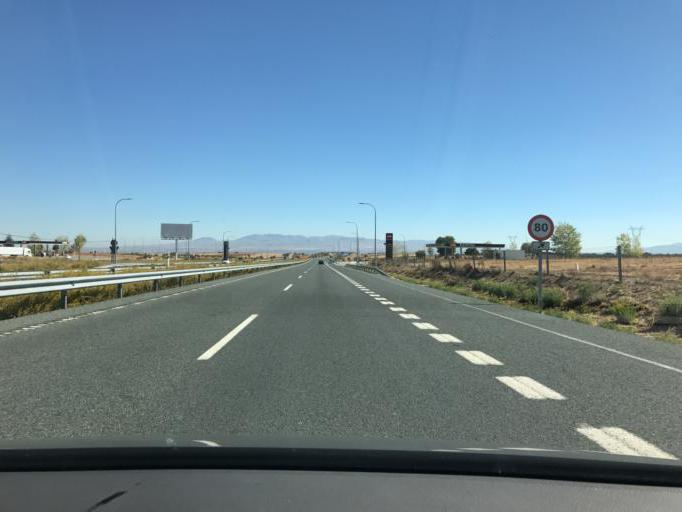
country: ES
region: Andalusia
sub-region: Provincia de Granada
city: Darro
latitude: 37.3212
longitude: -3.3001
